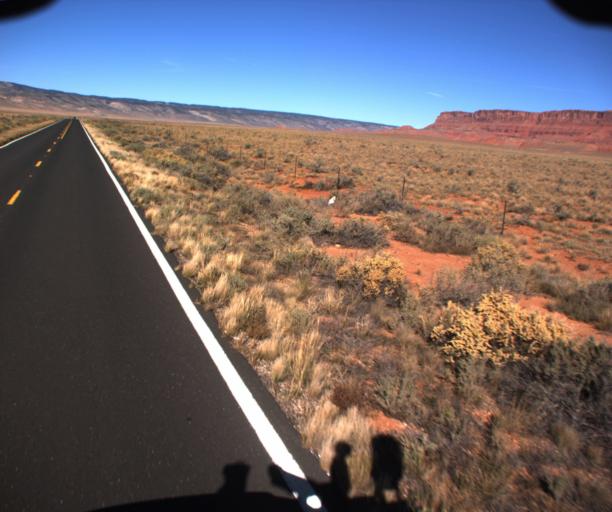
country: US
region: Arizona
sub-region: Coconino County
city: Page
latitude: 36.7076
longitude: -111.9586
